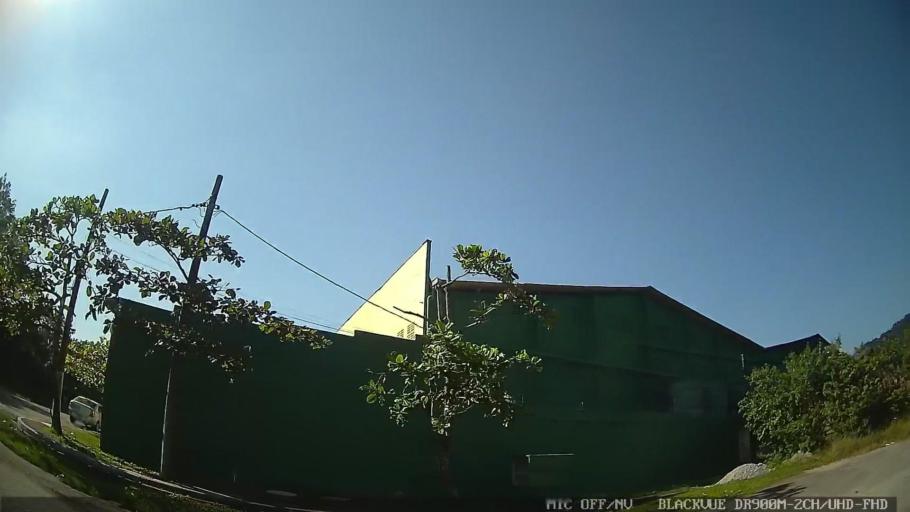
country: BR
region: Sao Paulo
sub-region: Guaruja
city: Guaruja
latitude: -24.0040
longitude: -46.2945
